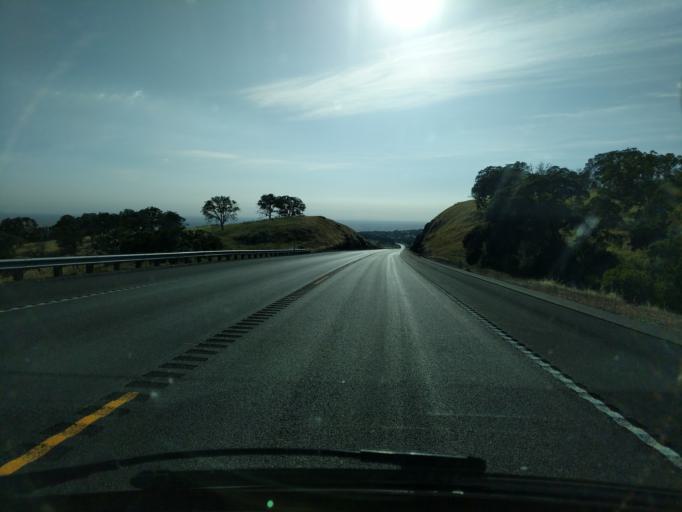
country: US
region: California
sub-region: Calaveras County
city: Copperopolis
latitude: 37.9422
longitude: -120.7119
